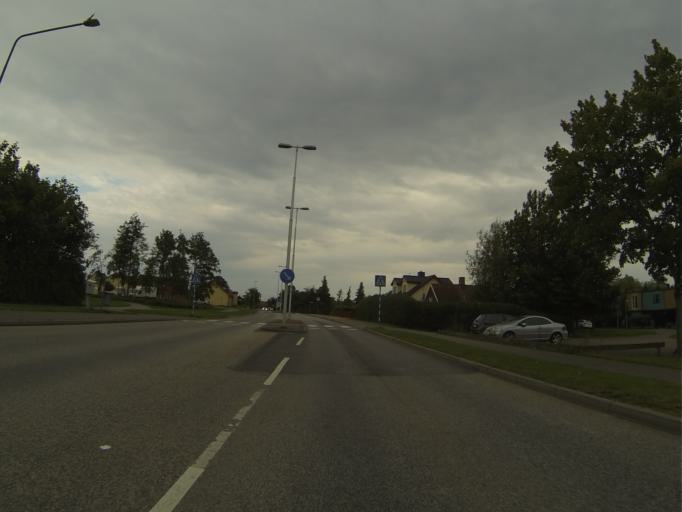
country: SE
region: Skane
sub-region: Staffanstorps Kommun
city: Staffanstorp
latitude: 55.6513
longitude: 13.2042
